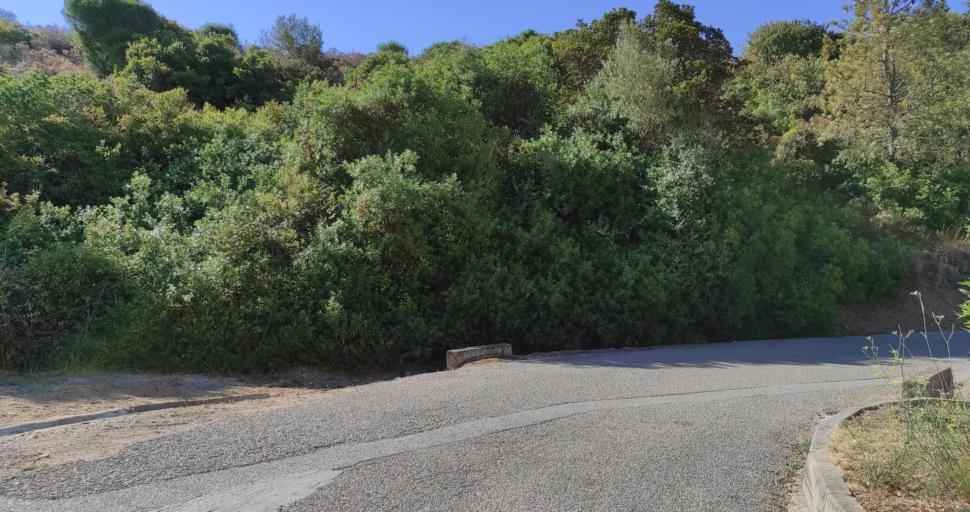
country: FR
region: Corsica
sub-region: Departement de la Corse-du-Sud
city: Alata
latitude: 41.9949
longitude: 8.6719
